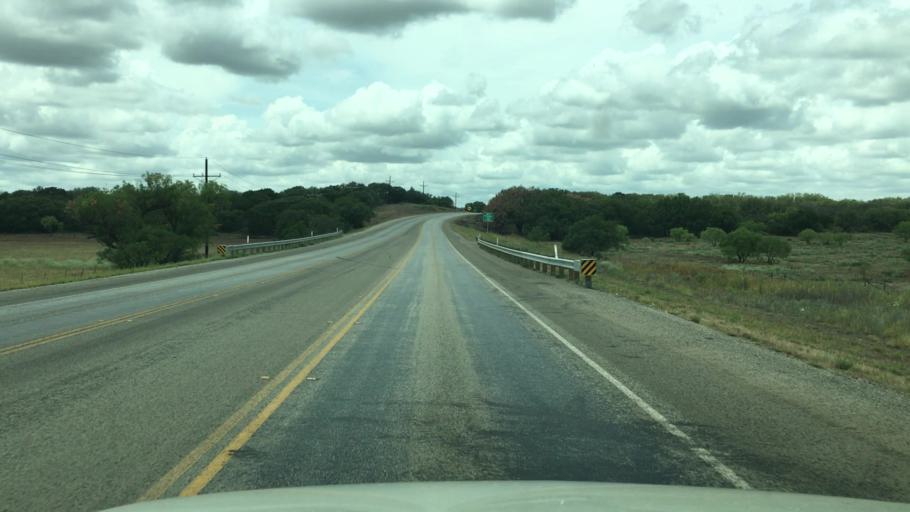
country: US
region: Texas
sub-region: McCulloch County
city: Brady
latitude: 31.0036
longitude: -99.1953
